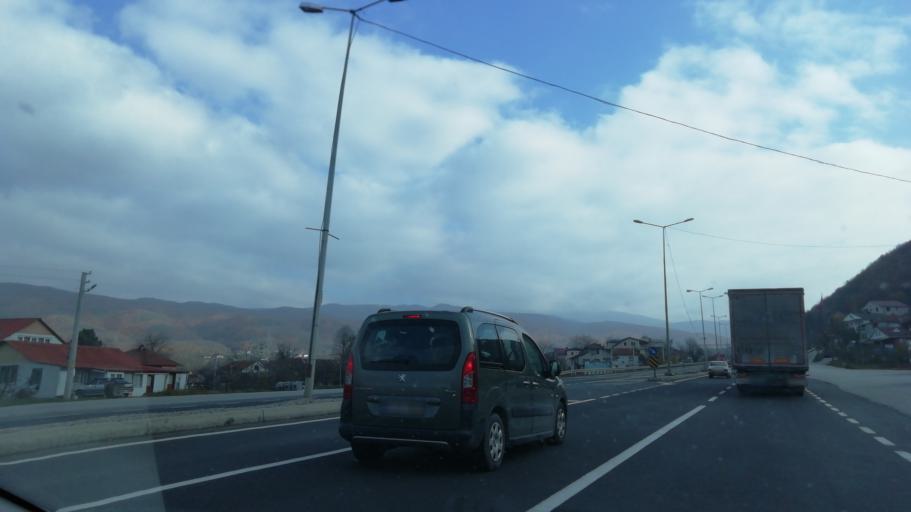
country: TR
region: Duzce
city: Kaynasli
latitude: 40.7725
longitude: 31.3296
